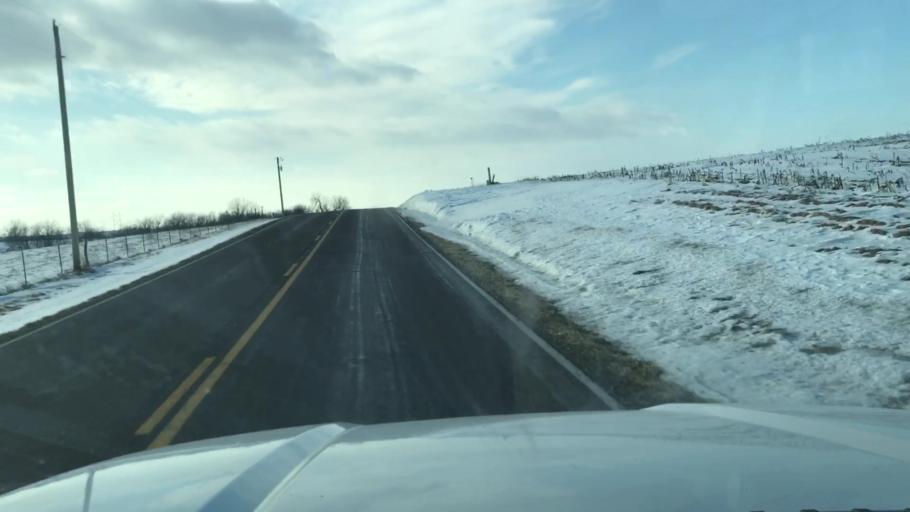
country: US
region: Missouri
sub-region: Nodaway County
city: Maryville
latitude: 40.2017
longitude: -94.9316
